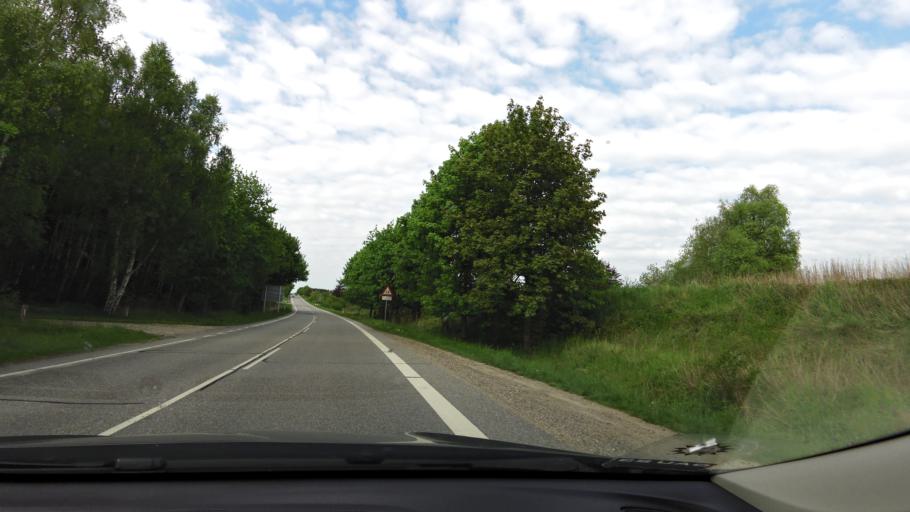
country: DK
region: South Denmark
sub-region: Nyborg Kommune
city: Nyborg
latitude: 55.3064
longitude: 10.7268
